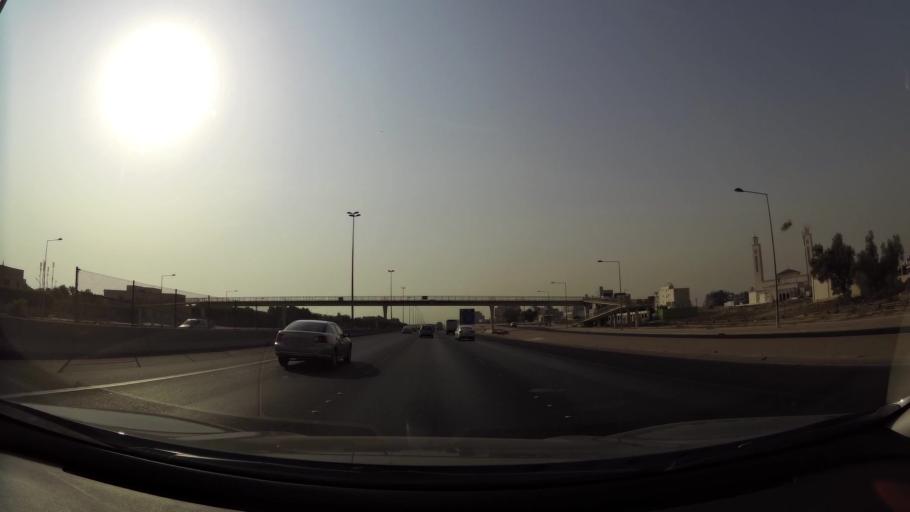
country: KW
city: Al Funaytis
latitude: 29.2349
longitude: 48.0961
